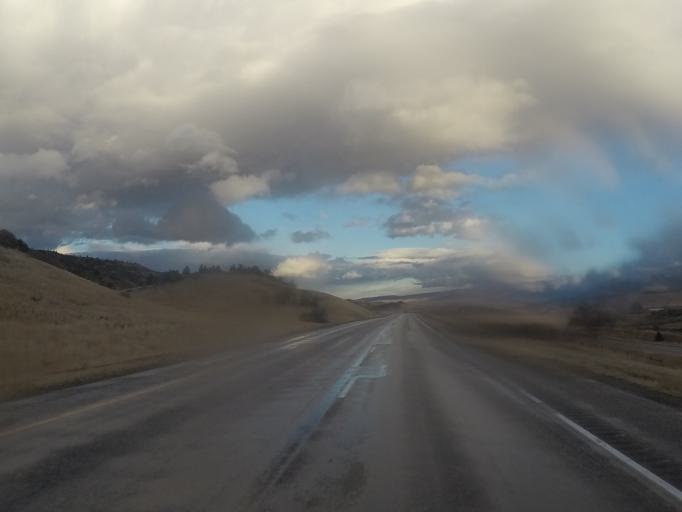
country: US
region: Montana
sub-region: Park County
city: Livingston
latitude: 45.6600
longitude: -110.6600
